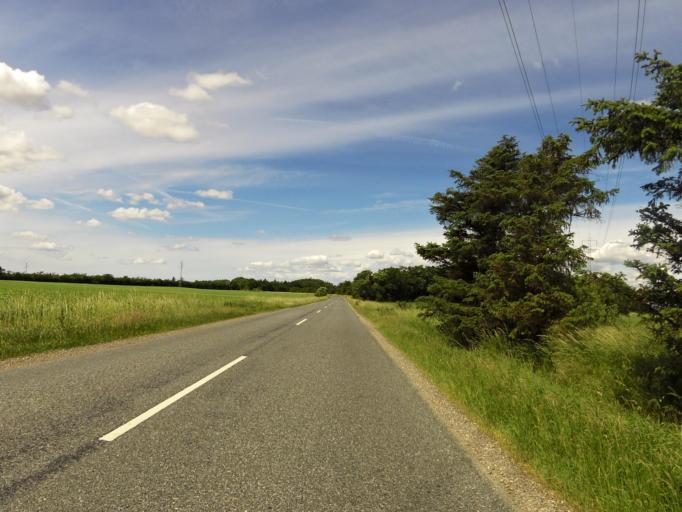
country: DK
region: South Denmark
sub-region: Esbjerg Kommune
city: Ribe
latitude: 55.2740
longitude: 8.8031
